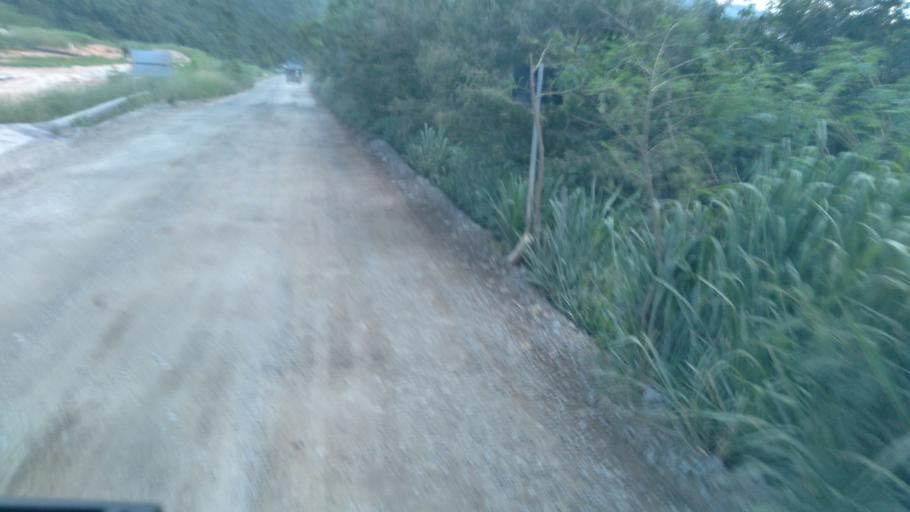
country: BR
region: Minas Gerais
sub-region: Santa Luzia
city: Santa Luzia
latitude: -19.8531
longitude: -43.8498
